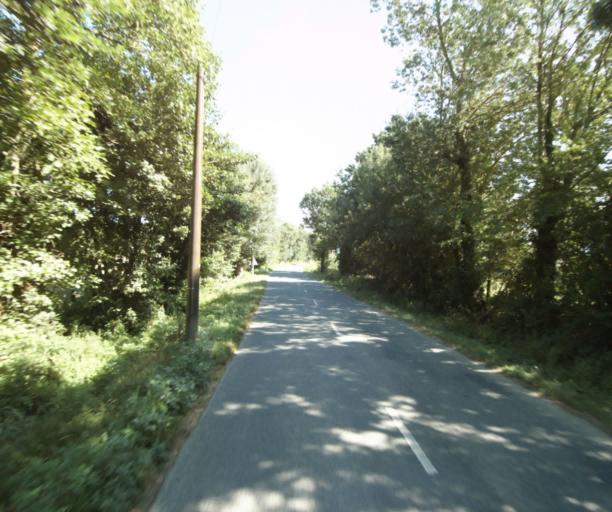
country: FR
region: Midi-Pyrenees
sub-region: Departement de la Haute-Garonne
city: Revel
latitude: 43.4844
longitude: 1.9862
